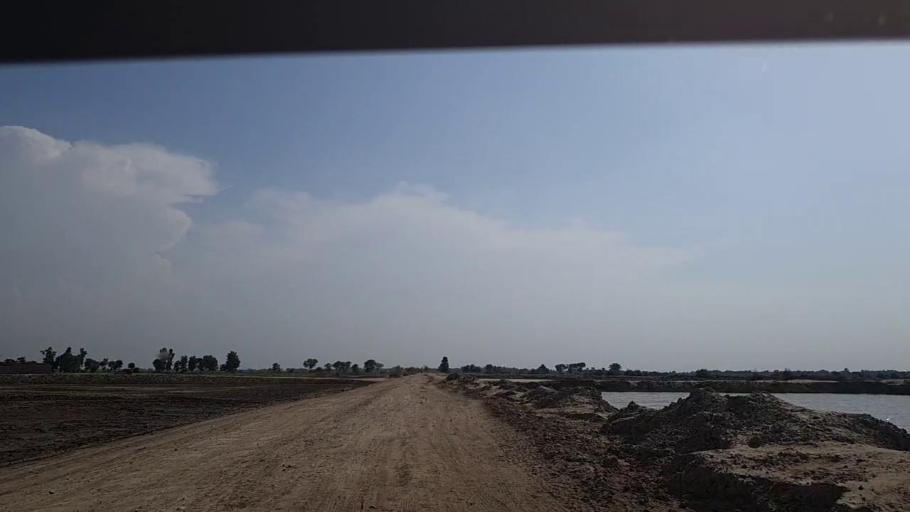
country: PK
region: Sindh
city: Khanpur
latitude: 27.8396
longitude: 69.3278
